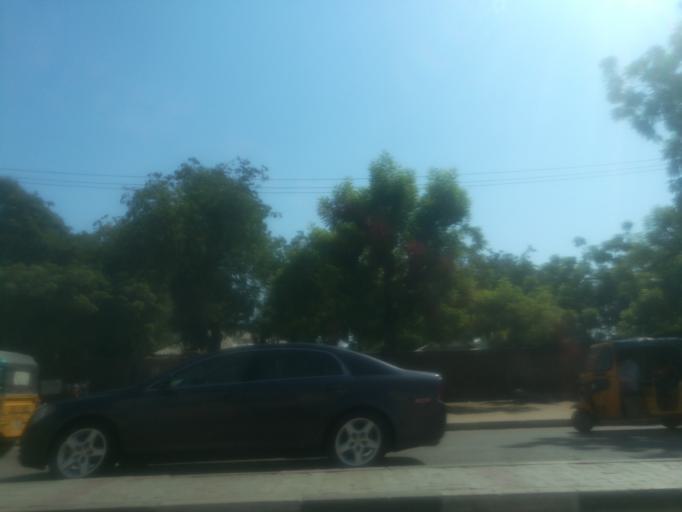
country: NG
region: Kano
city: Kano
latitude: 12.0107
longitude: 8.5428
